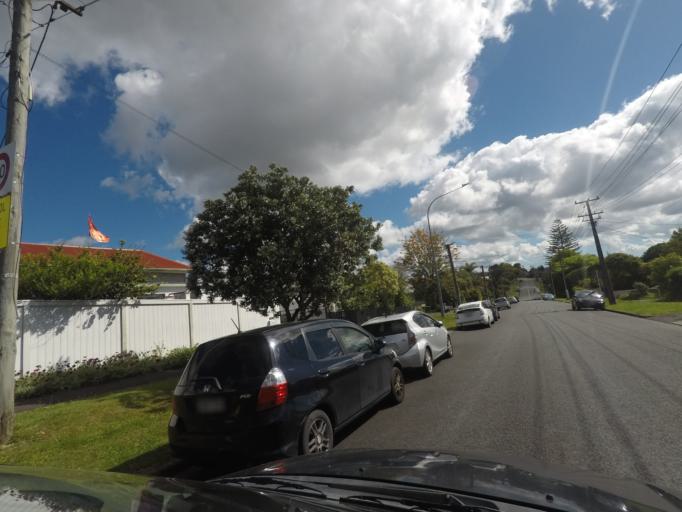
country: NZ
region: Auckland
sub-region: Auckland
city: Waitakere
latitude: -36.9135
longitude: 174.6663
